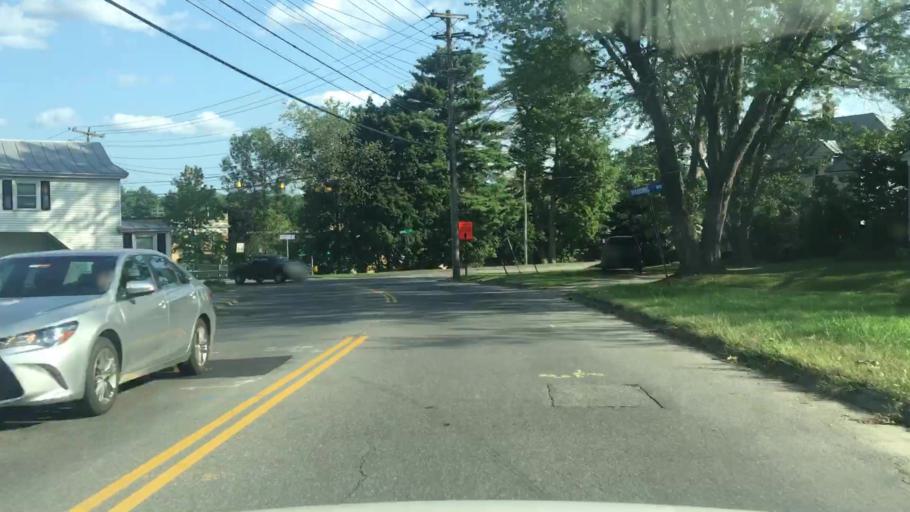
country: US
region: Maine
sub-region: Kennebec County
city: Waterville
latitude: 44.5488
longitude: -69.6433
